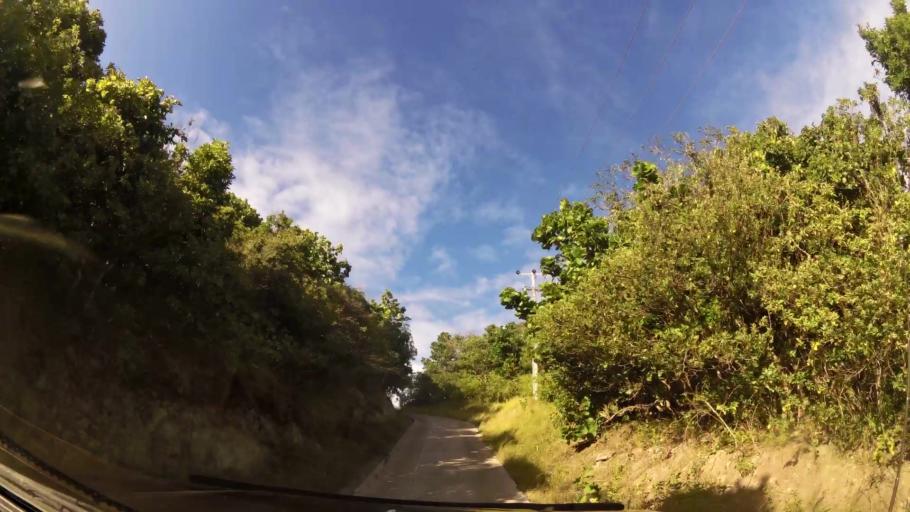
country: MS
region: Saint Peter
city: Brades
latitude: 16.8112
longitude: -62.1922
